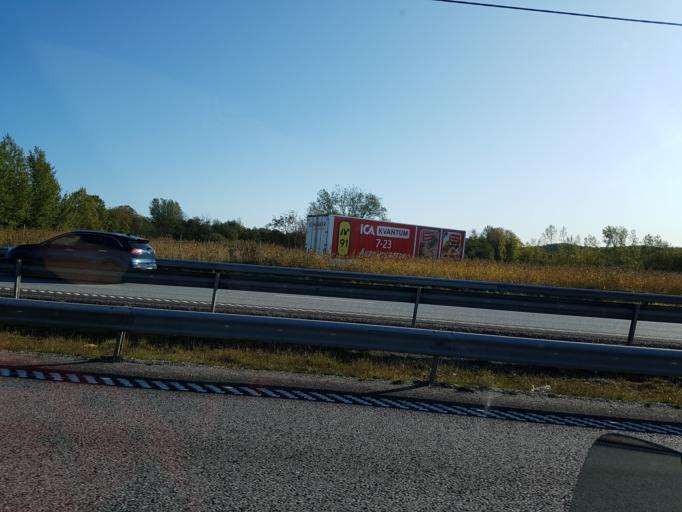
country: SE
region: Vaestra Goetaland
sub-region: Stenungsunds Kommun
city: Stora Hoga
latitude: 58.0176
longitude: 11.8437
